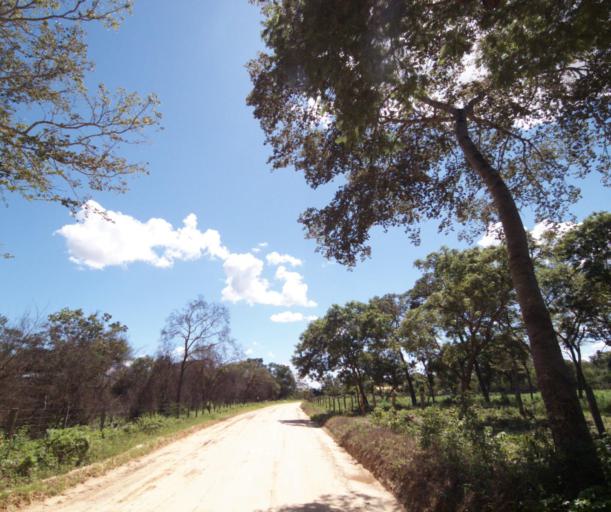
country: BR
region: Bahia
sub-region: Carinhanha
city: Carinhanha
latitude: -14.2324
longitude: -44.3080
